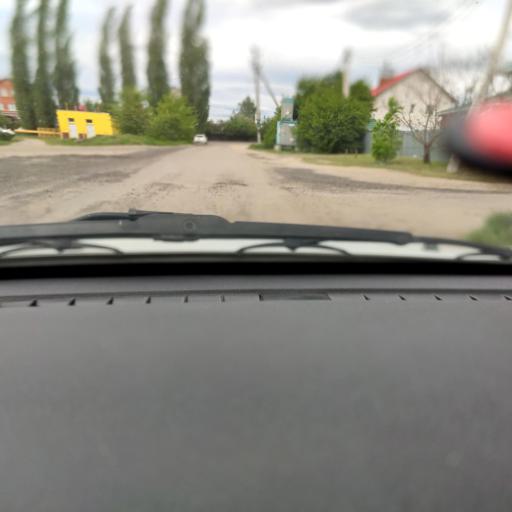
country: RU
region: Voronezj
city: Podgornoye
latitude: 51.7385
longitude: 39.1637
